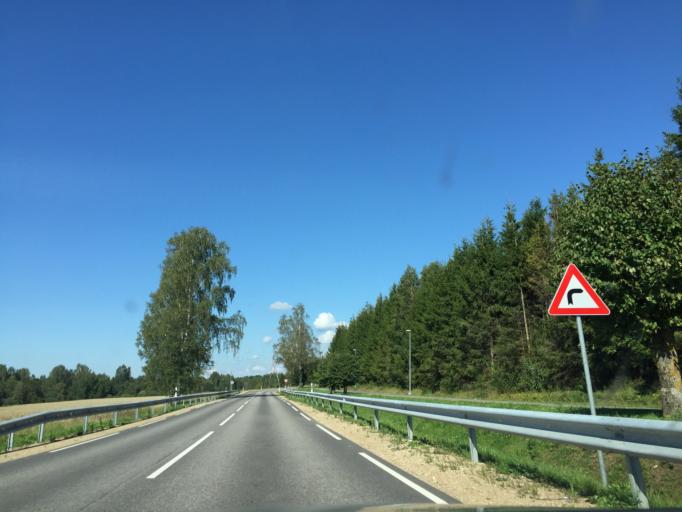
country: LV
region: Limbazu Rajons
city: Limbazi
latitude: 57.4948
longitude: 24.7093
